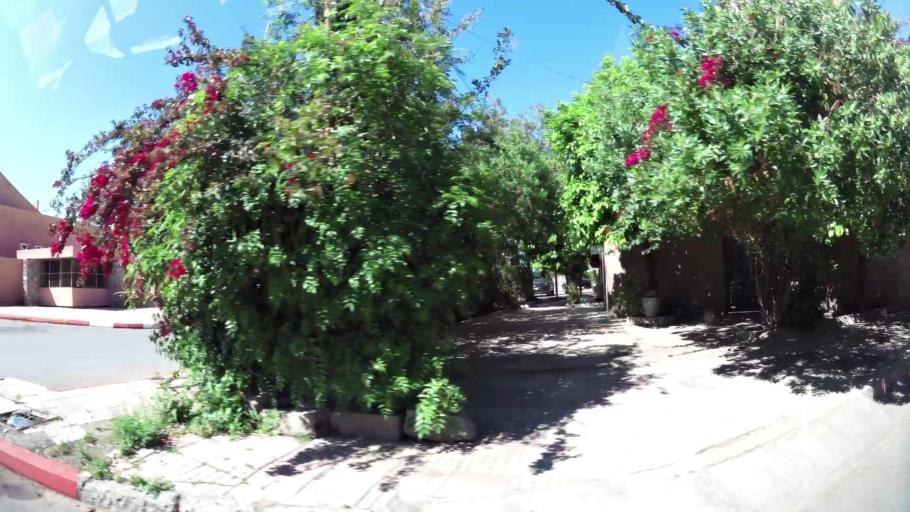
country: MA
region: Marrakech-Tensift-Al Haouz
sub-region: Marrakech
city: Marrakesh
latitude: 31.6416
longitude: -8.0073
